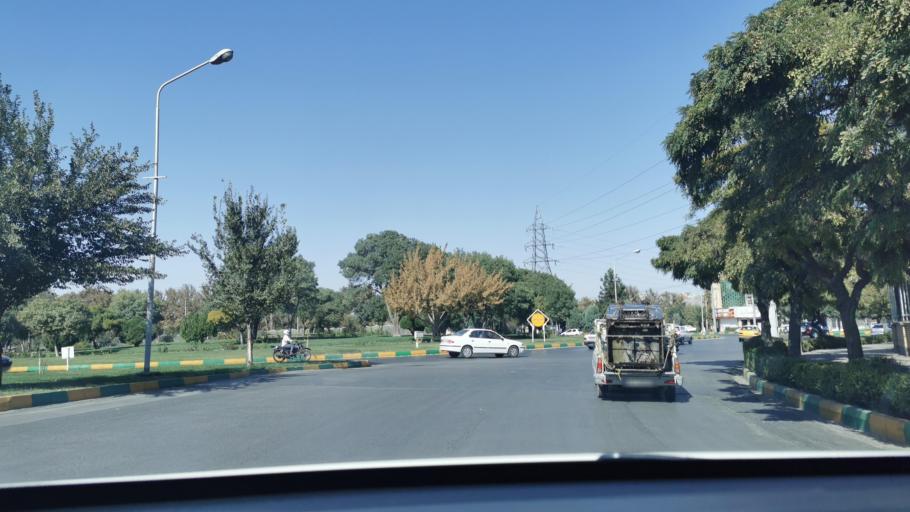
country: IR
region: Razavi Khorasan
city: Mashhad
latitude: 36.3285
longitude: 59.5793
